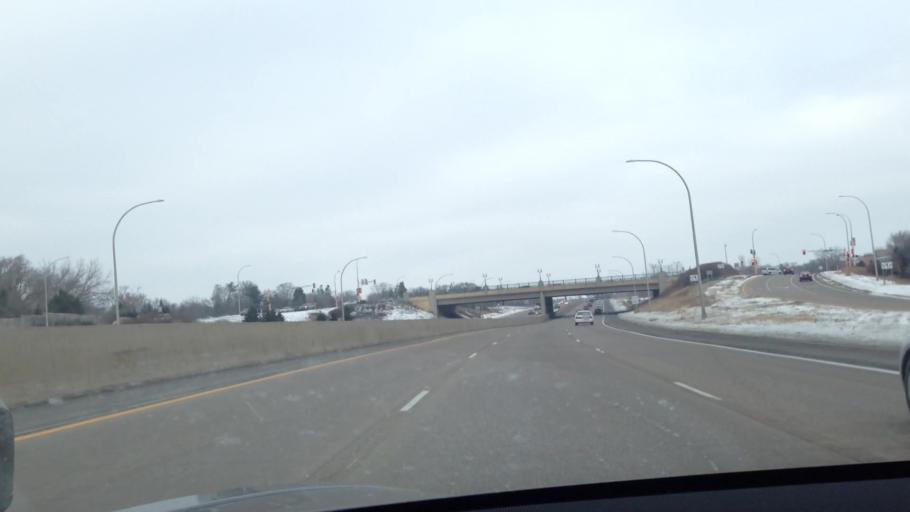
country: US
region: Minnesota
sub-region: Hennepin County
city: Golden Valley
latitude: 45.0189
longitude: -93.3492
